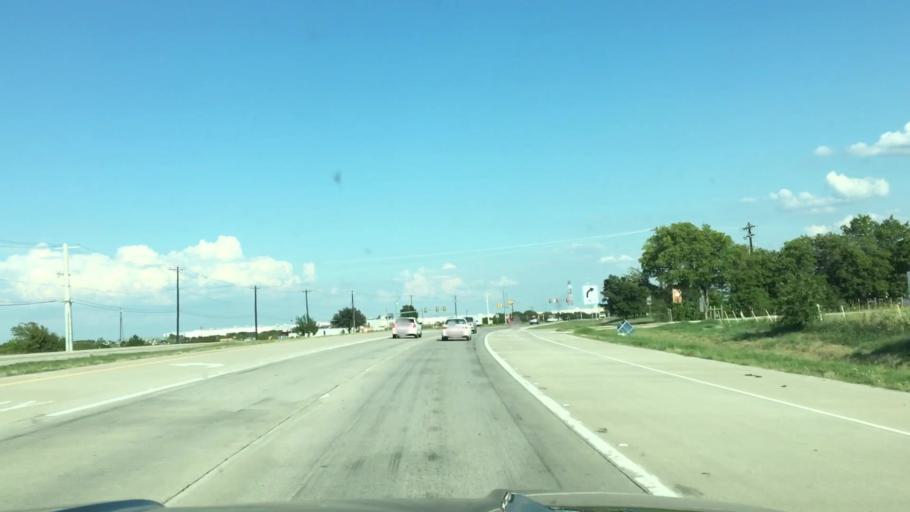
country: US
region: Texas
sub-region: Denton County
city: Justin
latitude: 33.0350
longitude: -97.3260
